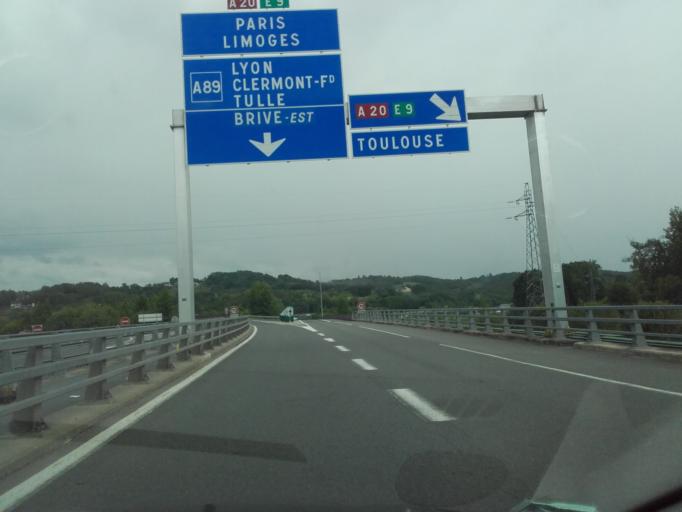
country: FR
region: Limousin
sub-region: Departement de la Correze
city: Ussac
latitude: 45.1884
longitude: 1.4899
